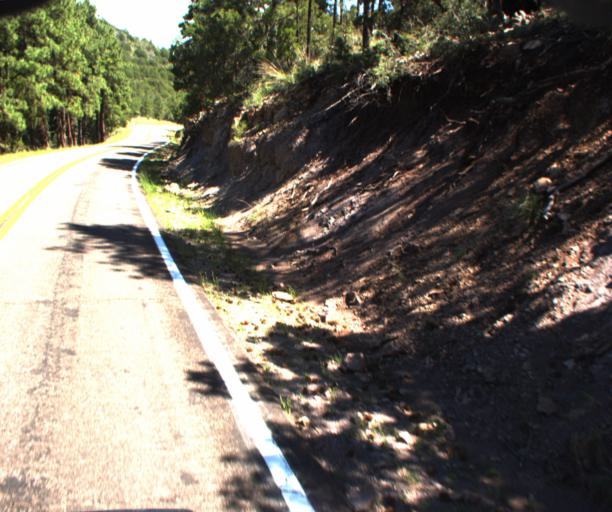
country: US
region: Arizona
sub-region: Greenlee County
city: Morenci
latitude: 33.2306
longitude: -109.3877
